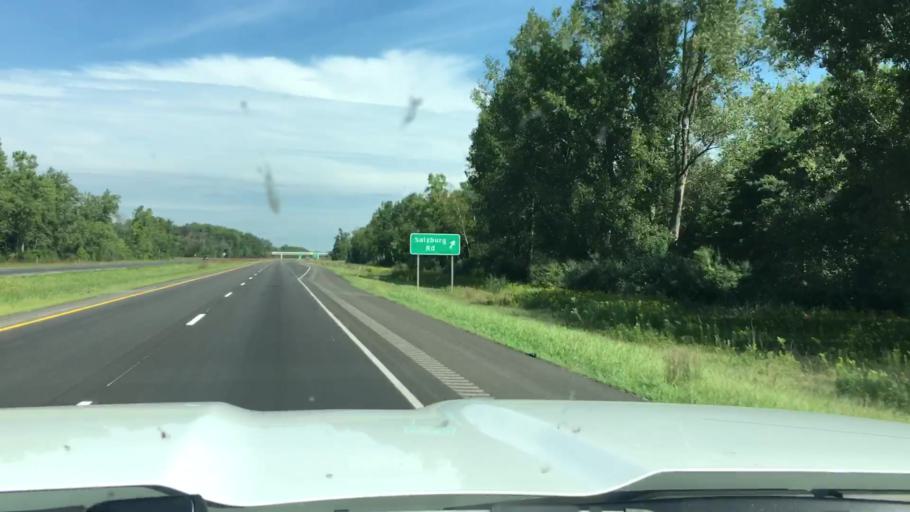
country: US
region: Michigan
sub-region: Saginaw County
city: Freeland
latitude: 43.5743
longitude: -84.1391
